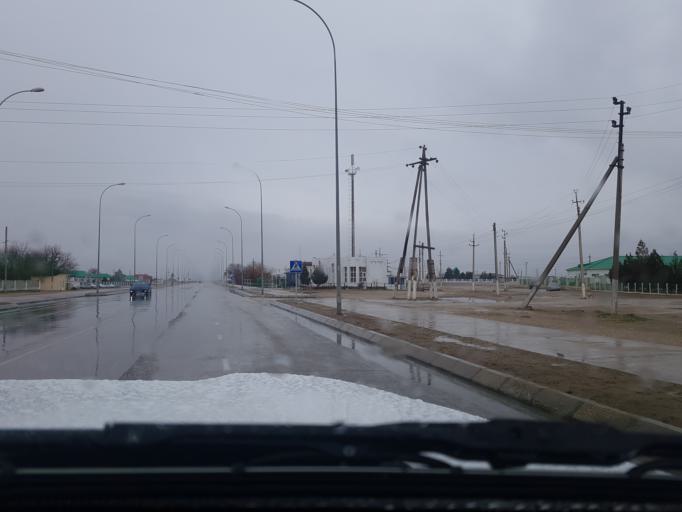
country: TM
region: Balkan
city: Balkanabat
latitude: 39.6327
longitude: 54.2359
